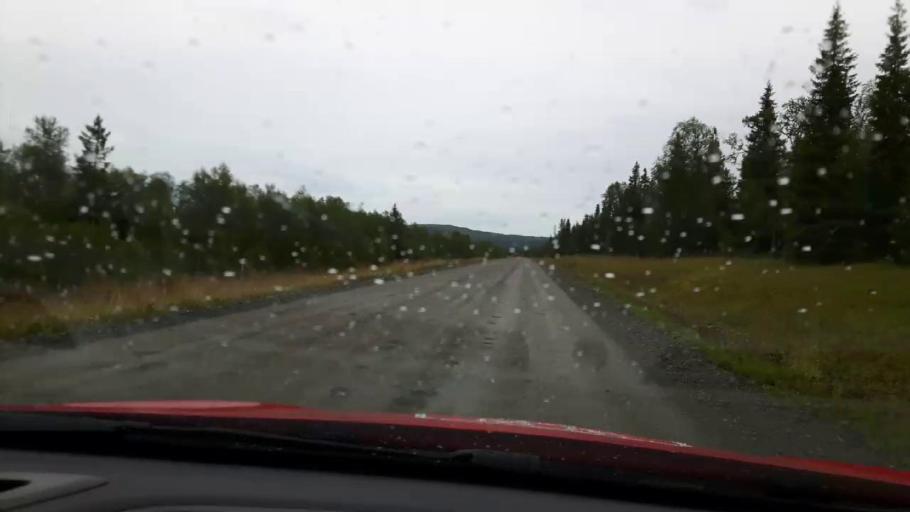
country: NO
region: Nord-Trondelag
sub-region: Meraker
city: Meraker
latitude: 63.5581
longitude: 12.3116
